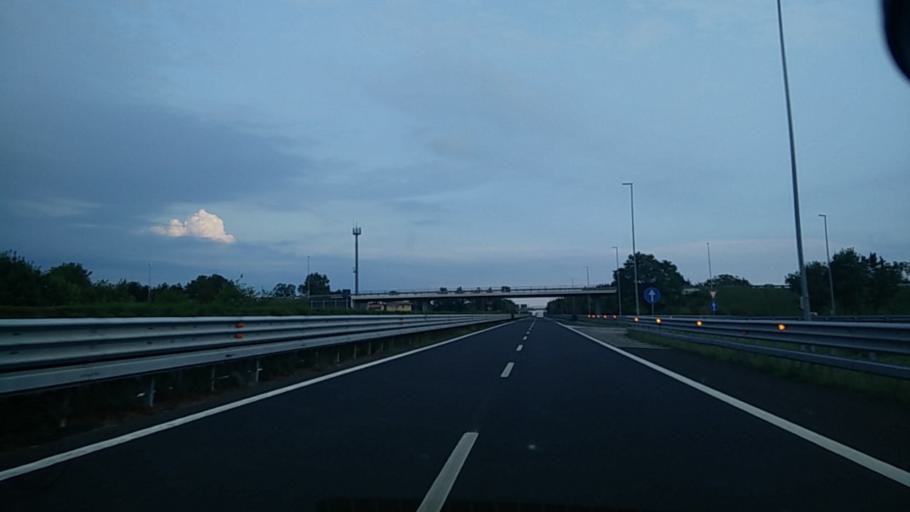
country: IT
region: Friuli Venezia Giulia
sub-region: Provincia di Udine
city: Zugliano-Terenzano-Cargnacco
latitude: 46.0108
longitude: 13.2218
